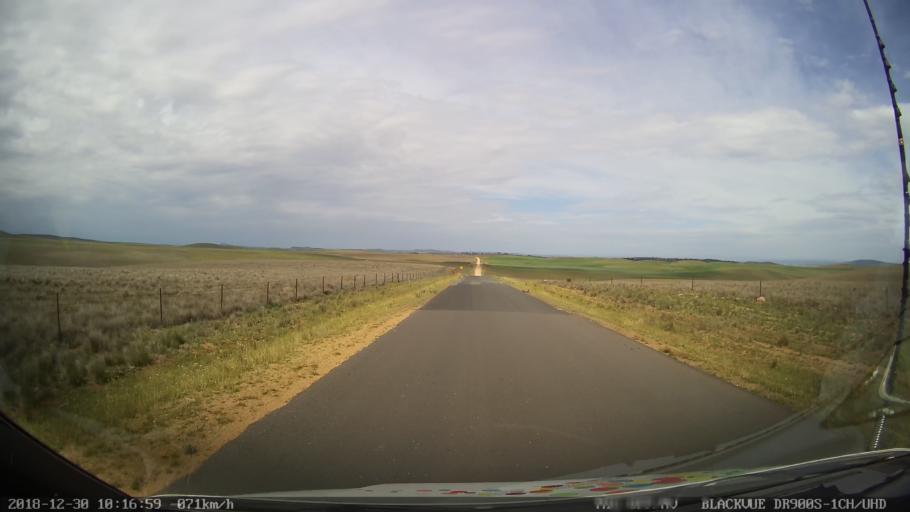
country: AU
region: New South Wales
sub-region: Snowy River
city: Berridale
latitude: -36.5471
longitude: 149.0269
